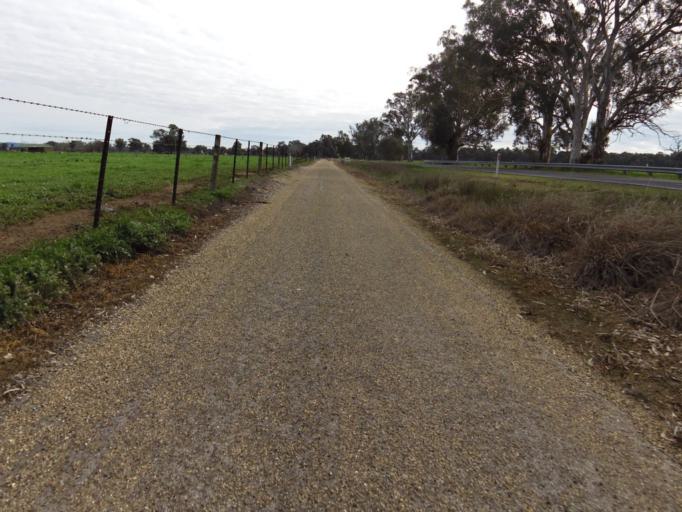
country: AU
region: Victoria
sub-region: Wangaratta
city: Wangaratta
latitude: -36.4150
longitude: 146.3542
